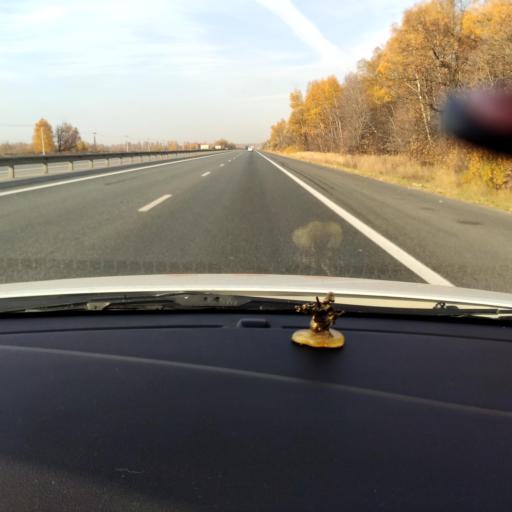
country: RU
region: Tatarstan
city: Osinovo
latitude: 55.9017
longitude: 48.9416
